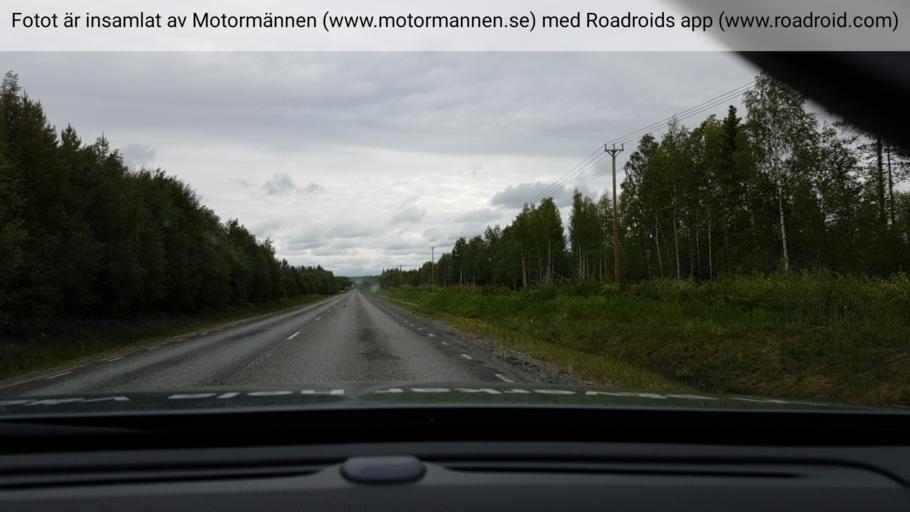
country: SE
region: Vaesterbotten
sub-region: Lycksele Kommun
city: Lycksele
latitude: 64.5337
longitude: 18.4767
